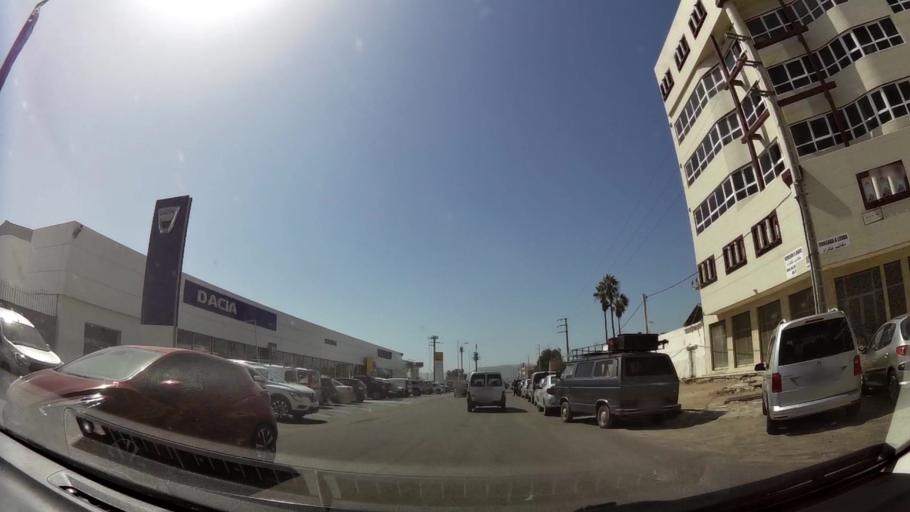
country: MA
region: Souss-Massa-Draa
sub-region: Agadir-Ida-ou-Tnan
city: Agadir
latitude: 30.4191
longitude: -9.5783
